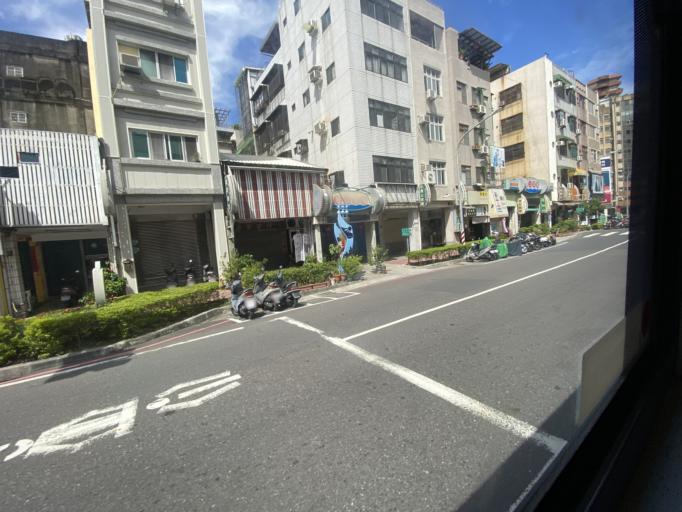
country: TW
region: Kaohsiung
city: Kaohsiung
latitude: 22.6243
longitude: 120.2821
